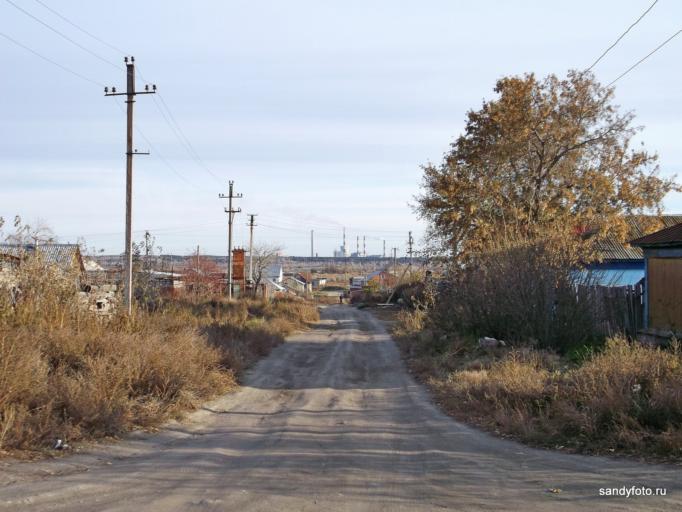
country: RU
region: Chelyabinsk
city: Troitsk
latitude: 54.0751
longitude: 61.5835
